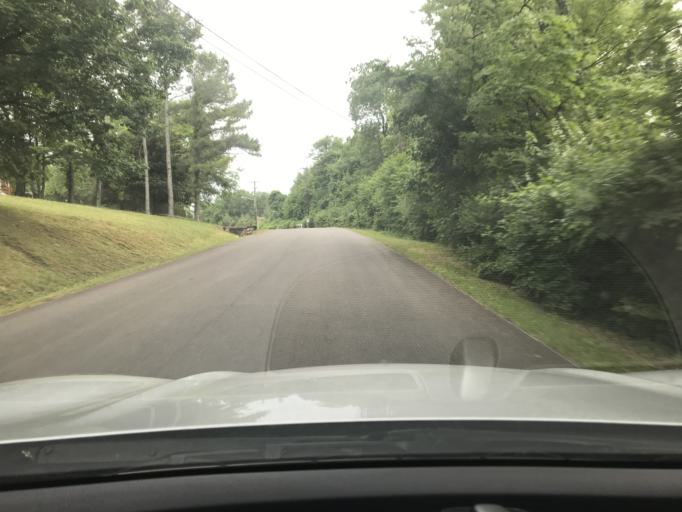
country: US
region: Tennessee
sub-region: Davidson County
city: Goodlettsville
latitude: 36.3121
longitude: -86.7223
